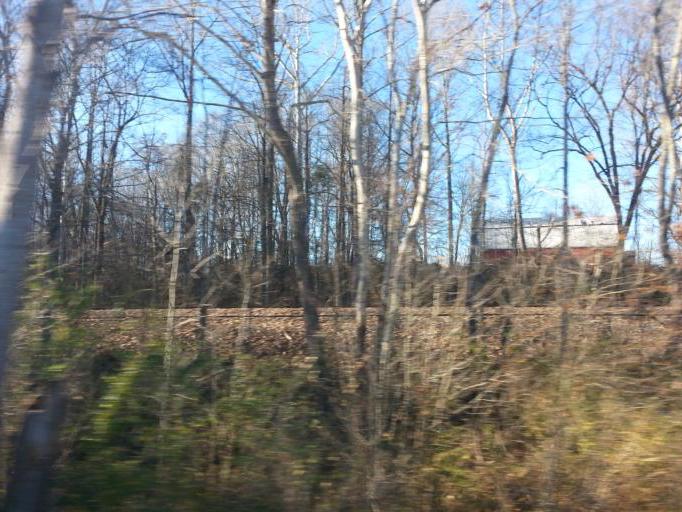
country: US
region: Tennessee
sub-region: Anderson County
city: Oak Ridge
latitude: 36.0479
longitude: -84.2464
